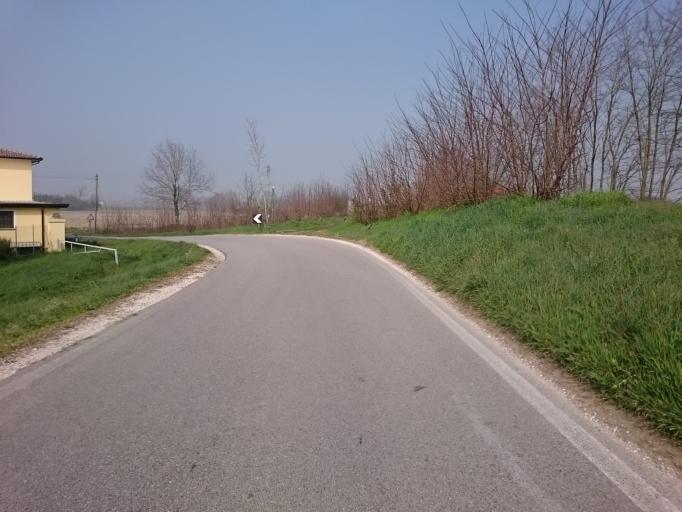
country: IT
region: Veneto
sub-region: Provincia di Padova
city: Due Carrare
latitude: 45.2719
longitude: 11.8199
